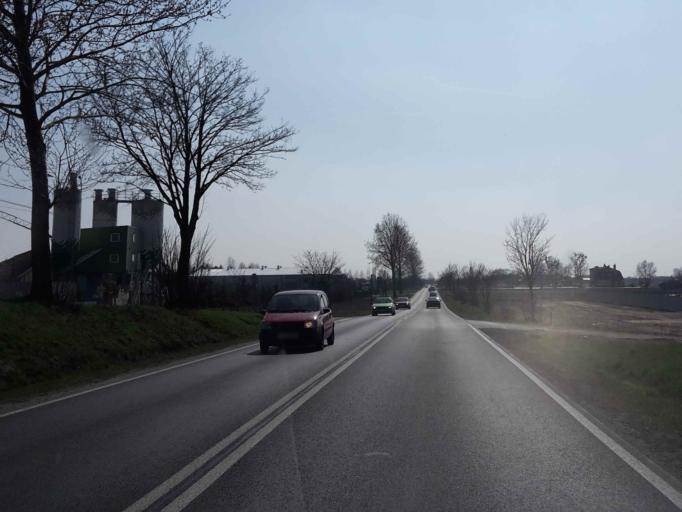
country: PL
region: Kujawsko-Pomorskie
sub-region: Powiat torunski
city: Lubicz Gorny
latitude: 53.0828
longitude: 18.7684
